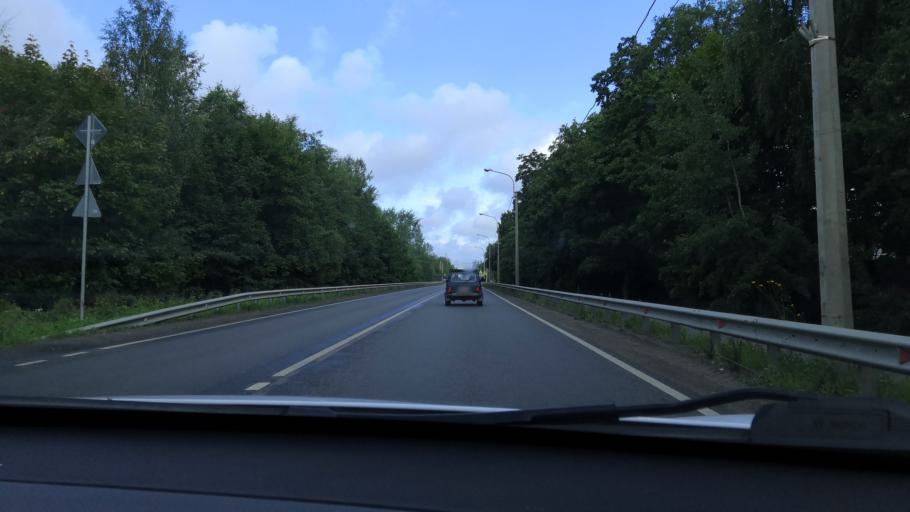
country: RU
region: St.-Petersburg
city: Tyarlevo
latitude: 59.6990
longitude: 30.4415
